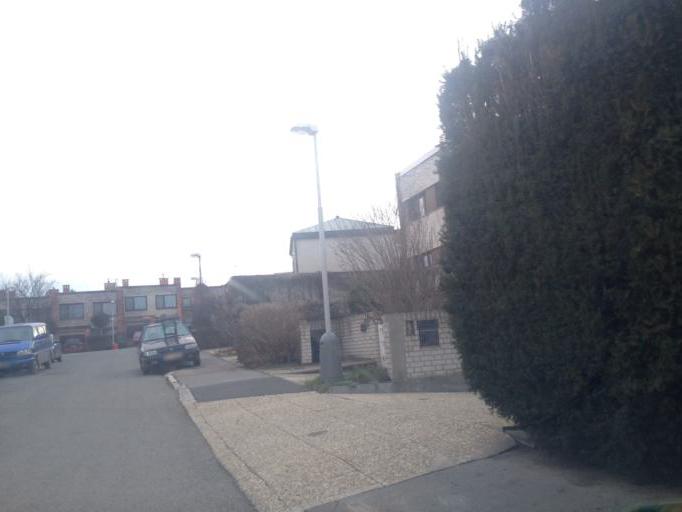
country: CZ
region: Praha
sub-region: Praha 1
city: Mala Strana
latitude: 50.1184
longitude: 14.3894
